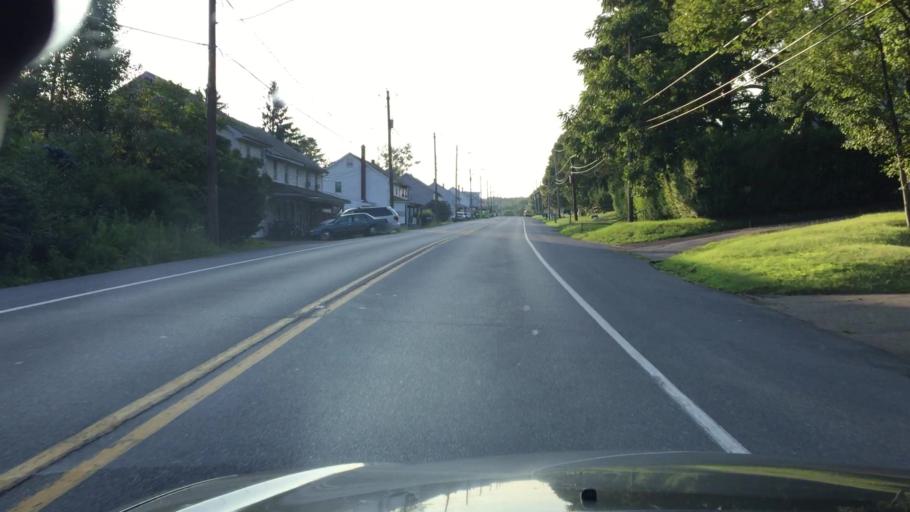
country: US
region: Pennsylvania
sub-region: Luzerne County
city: Hazleton
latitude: 40.9328
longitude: -75.9238
